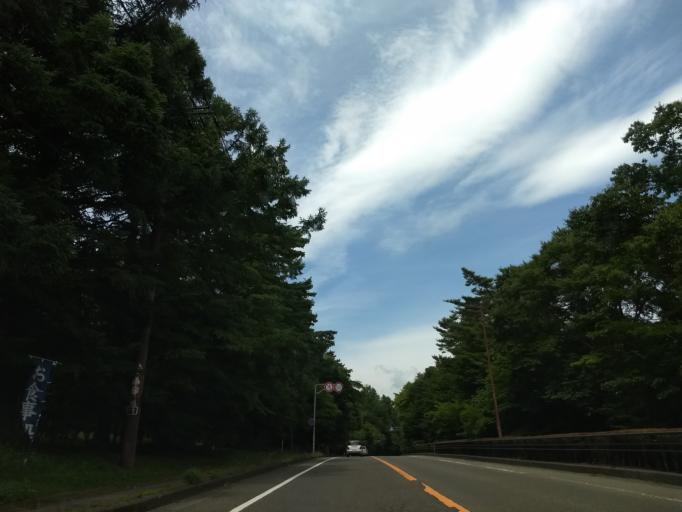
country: JP
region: Shizuoka
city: Gotemba
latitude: 35.4079
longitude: 138.8686
